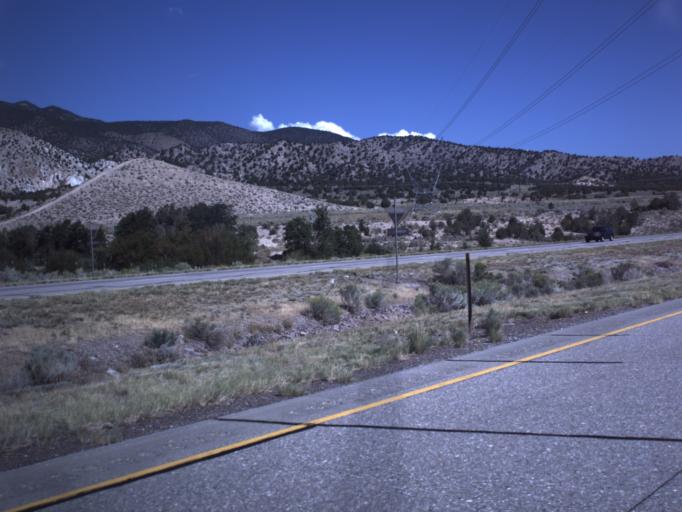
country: US
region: Utah
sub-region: Sevier County
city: Monroe
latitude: 38.5859
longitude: -112.2742
